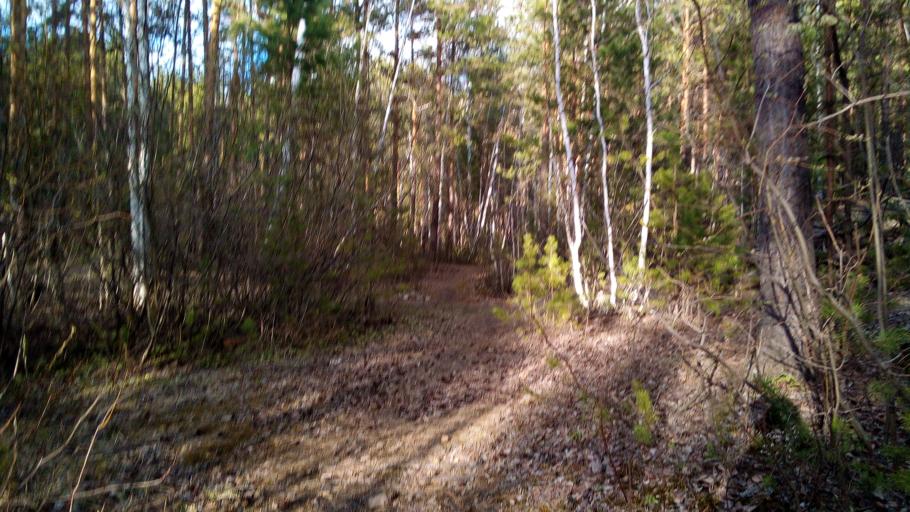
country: RU
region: Chelyabinsk
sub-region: Gorod Chelyabinsk
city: Chelyabinsk
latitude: 55.1647
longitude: 61.3250
